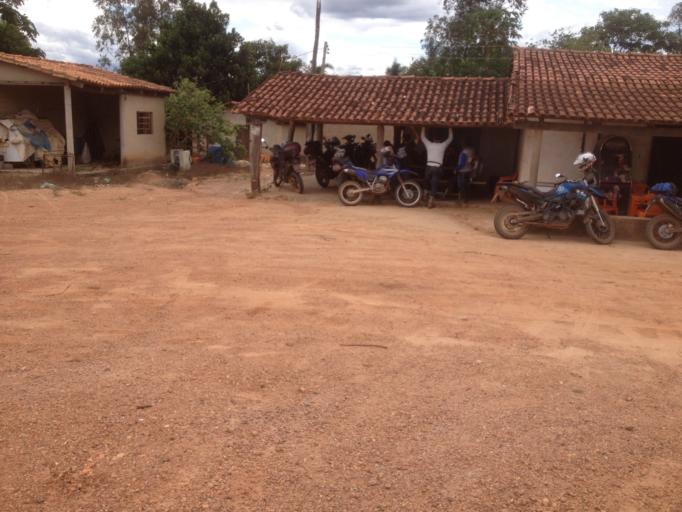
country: BR
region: Goias
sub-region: Silvania
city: Silvania
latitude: -16.4739
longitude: -48.4519
